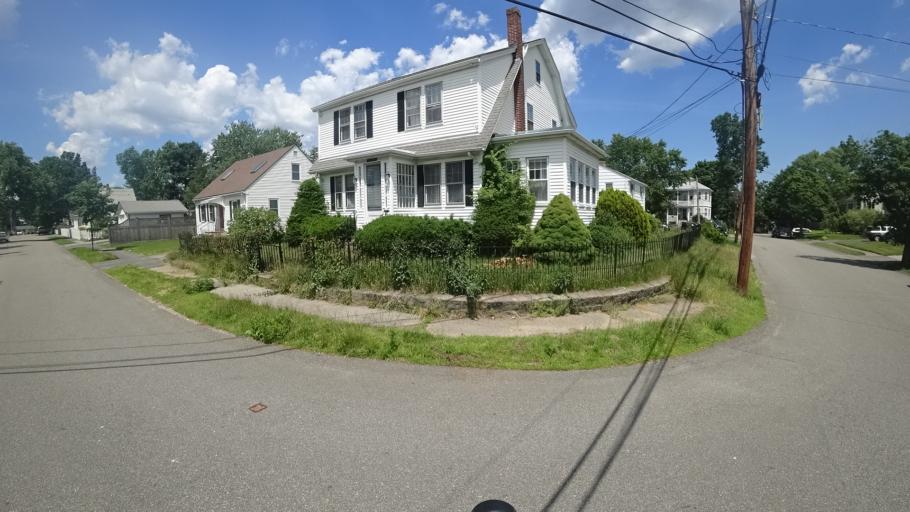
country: US
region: Massachusetts
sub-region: Norfolk County
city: Dedham
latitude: 42.2729
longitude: -71.1791
